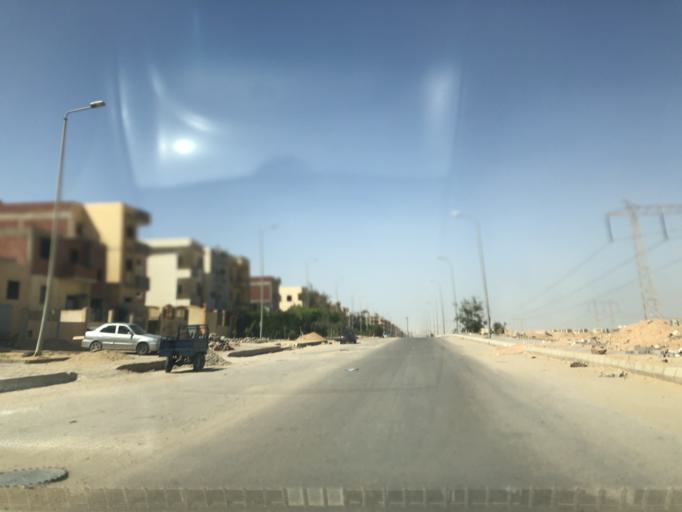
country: EG
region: Al Jizah
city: Madinat Sittah Uktubar
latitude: 29.9142
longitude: 31.0503
